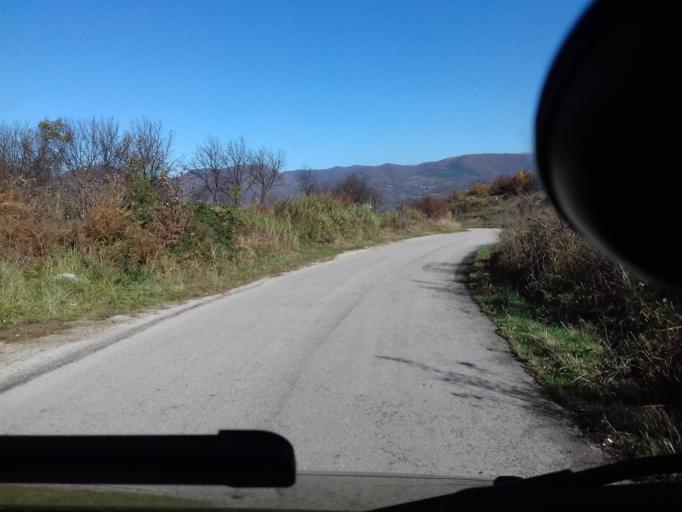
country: BA
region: Federation of Bosnia and Herzegovina
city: Zenica
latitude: 44.1819
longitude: 17.9064
